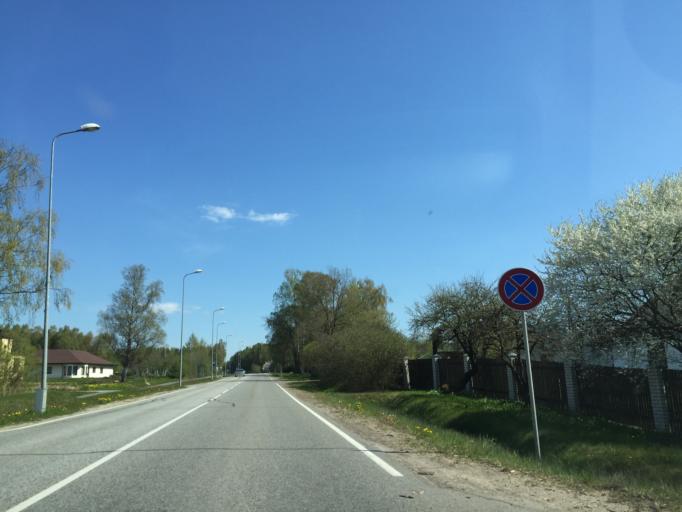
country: LV
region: Saulkrastu
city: Saulkrasti
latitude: 57.3193
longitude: 24.4220
